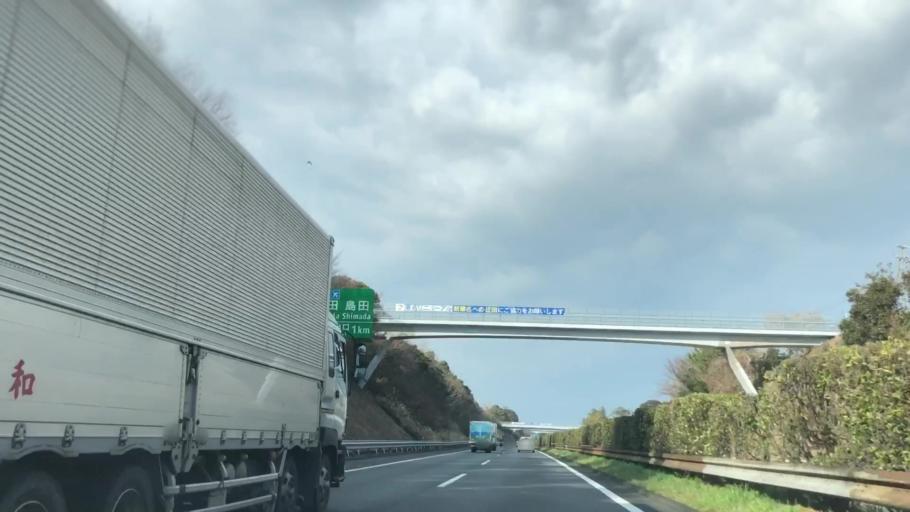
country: JP
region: Shizuoka
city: Shimada
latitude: 34.7805
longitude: 138.2295
